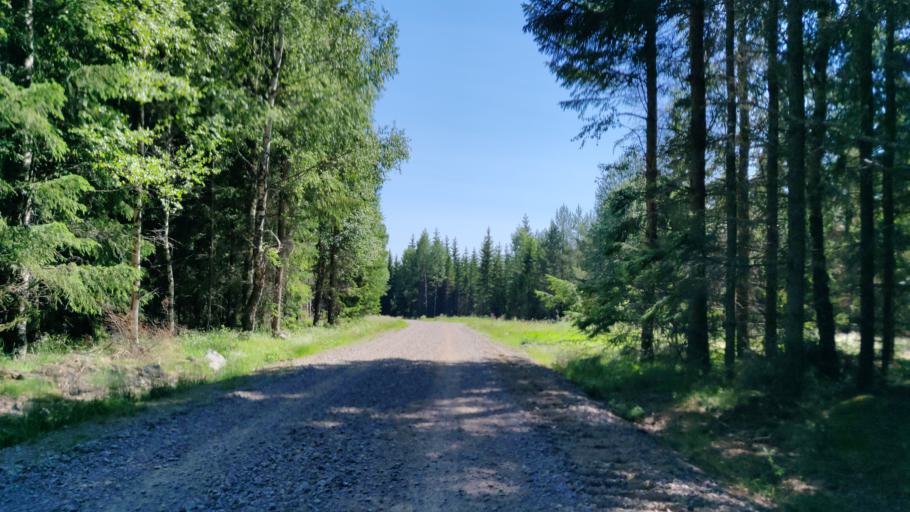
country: SE
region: Vaermland
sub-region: Hagfors Kommun
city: Hagfors
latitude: 59.9805
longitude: 13.5978
